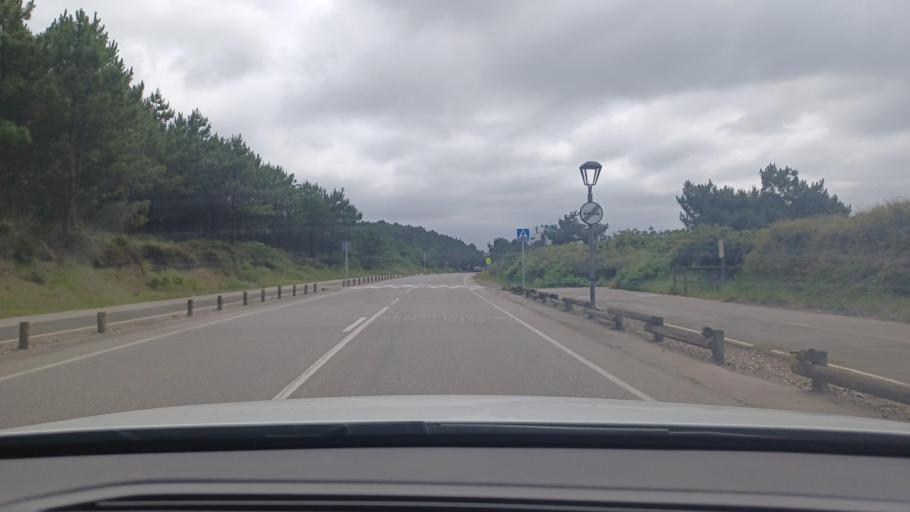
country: ES
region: Asturias
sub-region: Province of Asturias
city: Aviles
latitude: 43.5817
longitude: -5.9453
